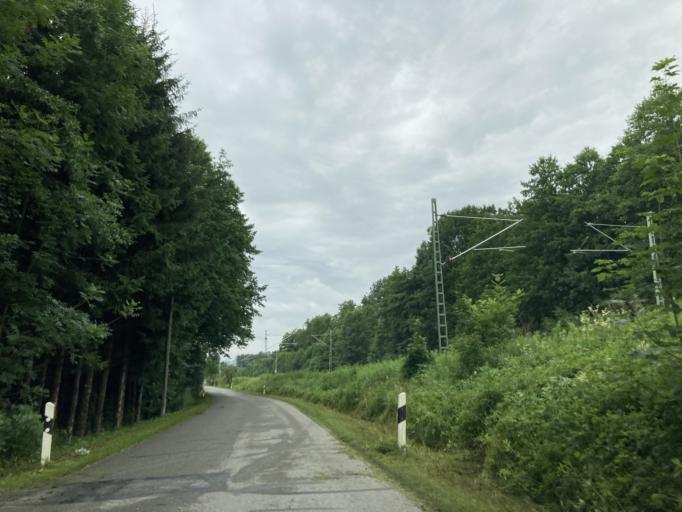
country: DE
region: Bavaria
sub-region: Upper Bavaria
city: Prutting
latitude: 47.8718
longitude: 12.2242
